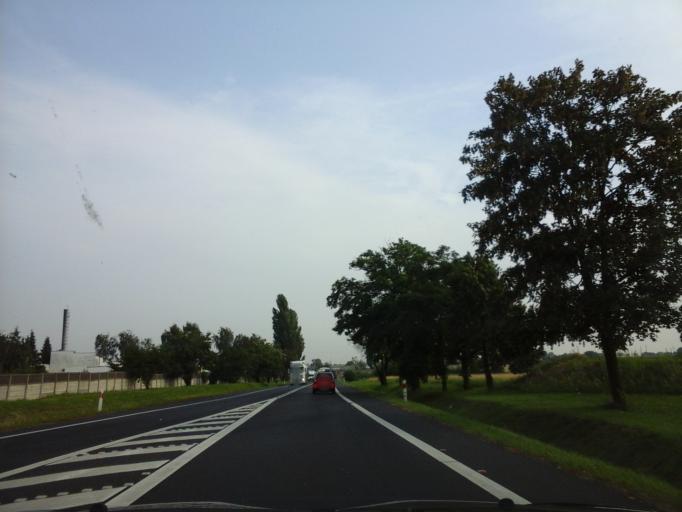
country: PL
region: Greater Poland Voivodeship
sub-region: Powiat koscianski
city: Koscian
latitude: 52.0788
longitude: 16.6203
